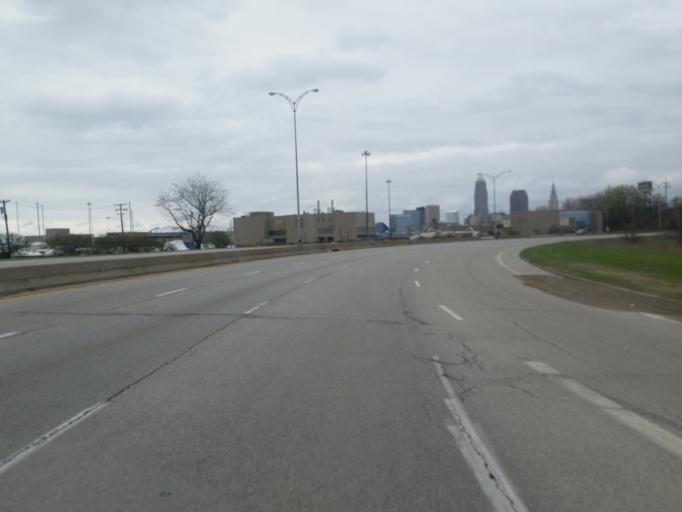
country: US
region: Ohio
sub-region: Cuyahoga County
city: Cleveland
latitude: 41.4911
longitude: -81.7302
